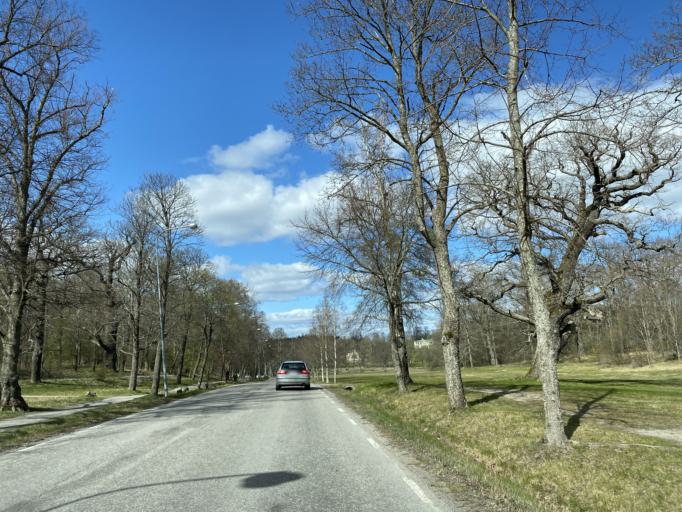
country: SE
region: Stockholm
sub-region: Nacka Kommun
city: Nacka
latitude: 59.3261
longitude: 18.1336
